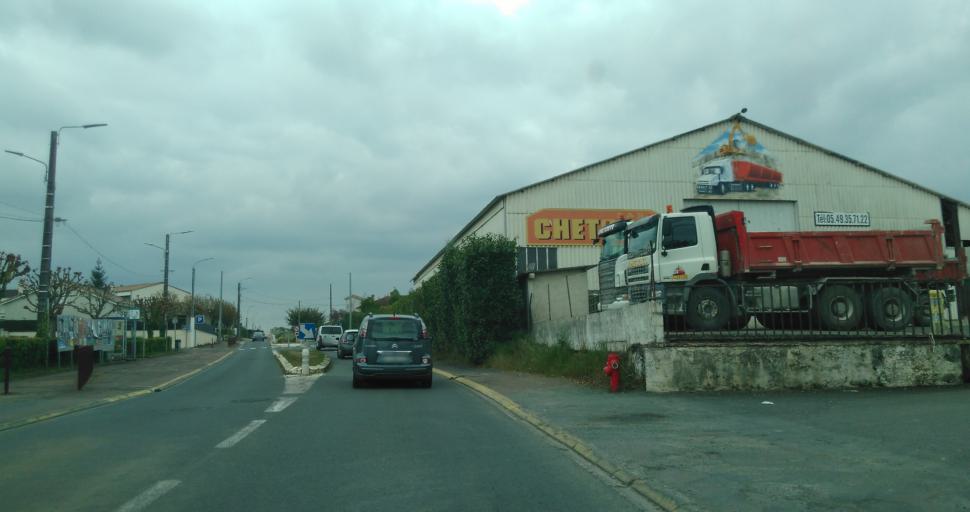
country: FR
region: Poitou-Charentes
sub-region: Departement des Deux-Sevres
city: Magne
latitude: 46.3153
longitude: -0.5468
